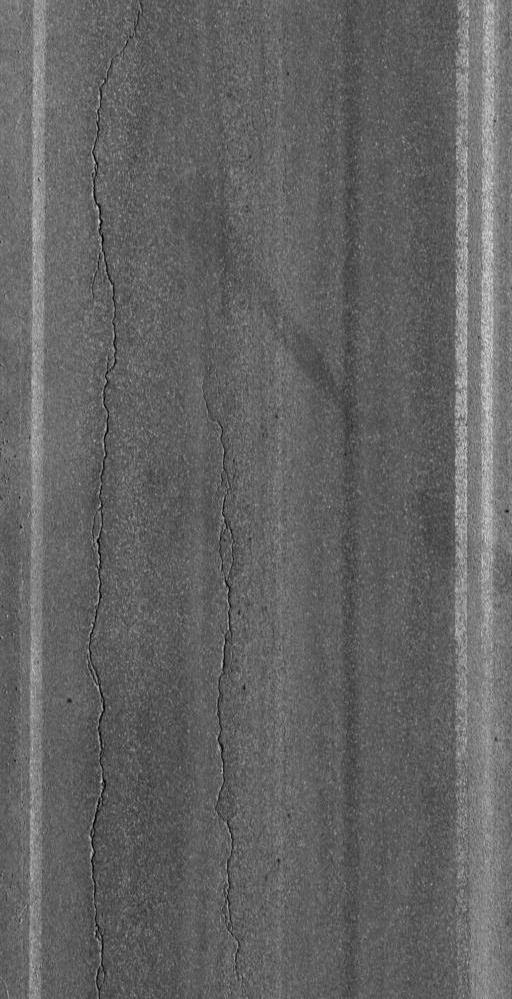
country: US
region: Vermont
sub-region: Chittenden County
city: Essex Junction
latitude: 44.4471
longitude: -73.1276
